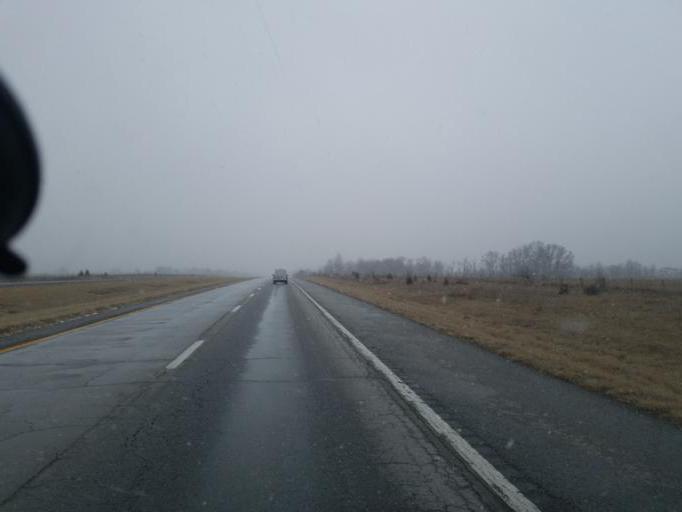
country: US
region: Missouri
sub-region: Macon County
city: La Plata
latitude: 39.9805
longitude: -92.4761
